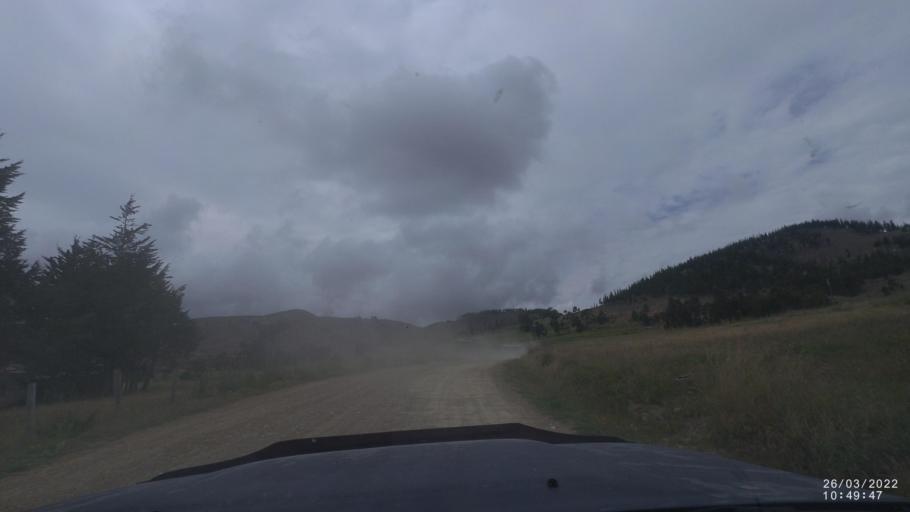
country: BO
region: Cochabamba
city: Tarata
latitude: -17.5042
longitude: -66.0344
